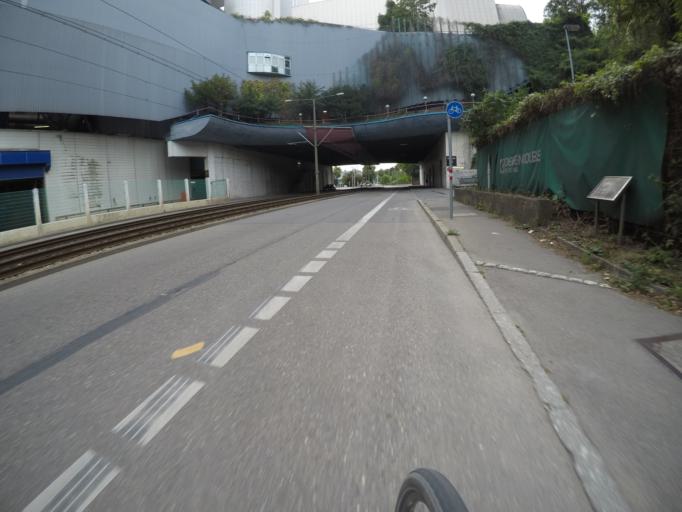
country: DE
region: Baden-Wuerttemberg
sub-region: Regierungsbezirk Stuttgart
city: Stuttgart Muehlhausen
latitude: 48.8155
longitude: 9.2196
